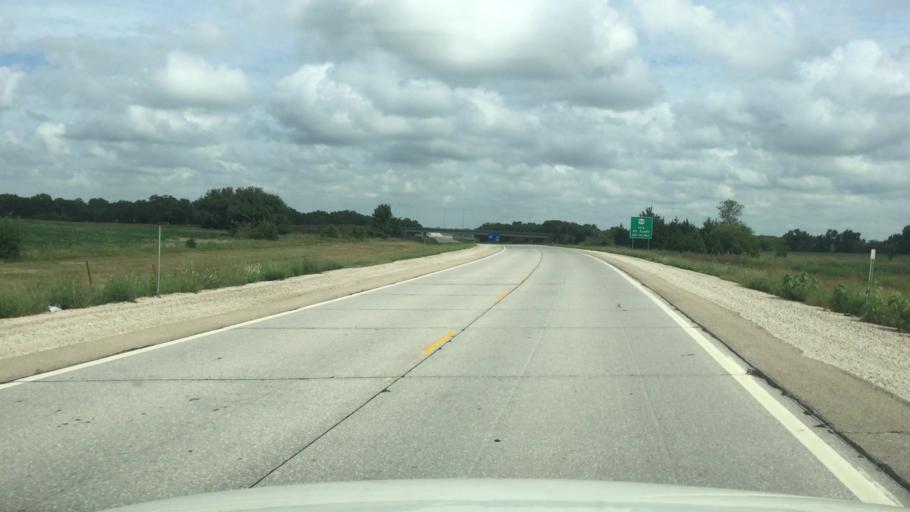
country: US
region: Kansas
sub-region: Allen County
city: Iola
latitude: 37.9106
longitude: -95.3797
